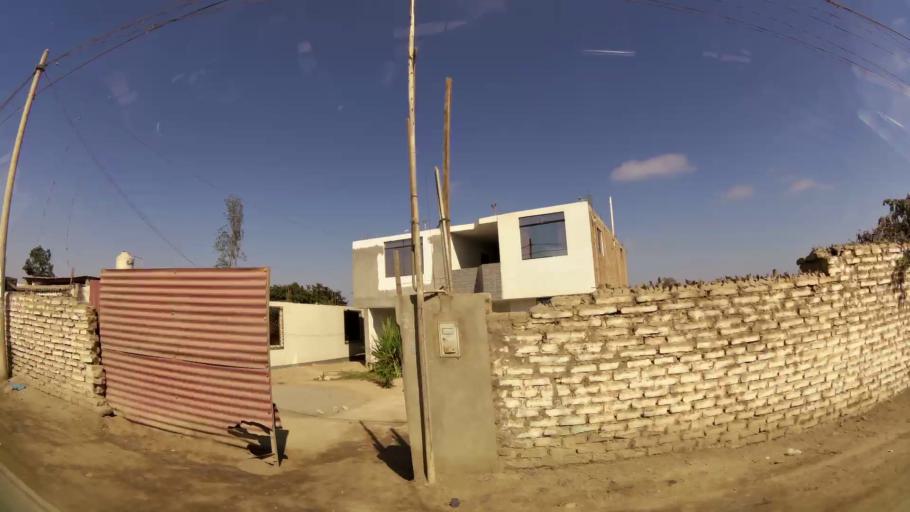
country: PE
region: Ica
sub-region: Provincia de Chincha
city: Sunampe
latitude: -13.4207
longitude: -76.1665
